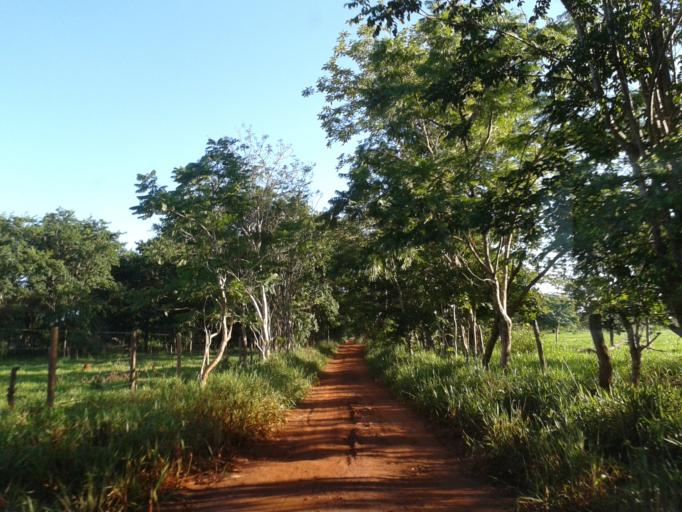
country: BR
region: Minas Gerais
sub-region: Santa Vitoria
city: Santa Vitoria
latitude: -19.1190
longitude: -50.5392
